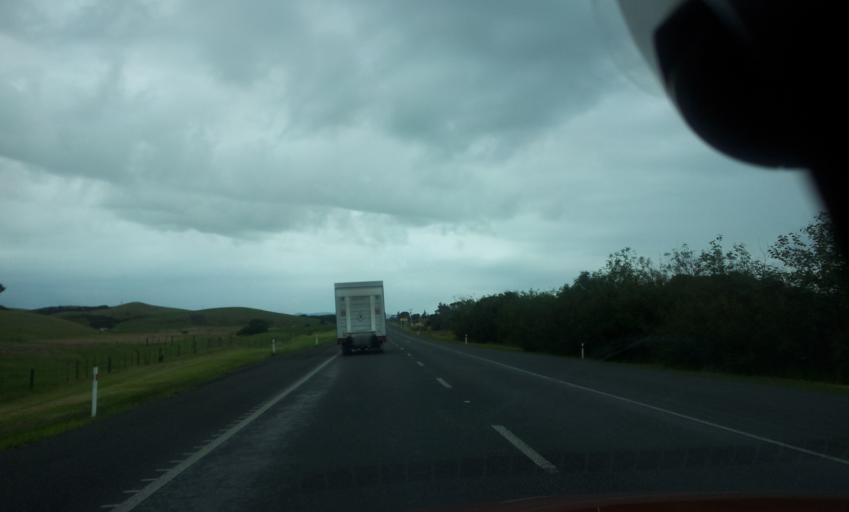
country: NZ
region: Northland
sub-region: Whangarei
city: Ruakaka
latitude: -35.9332
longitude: 174.4552
